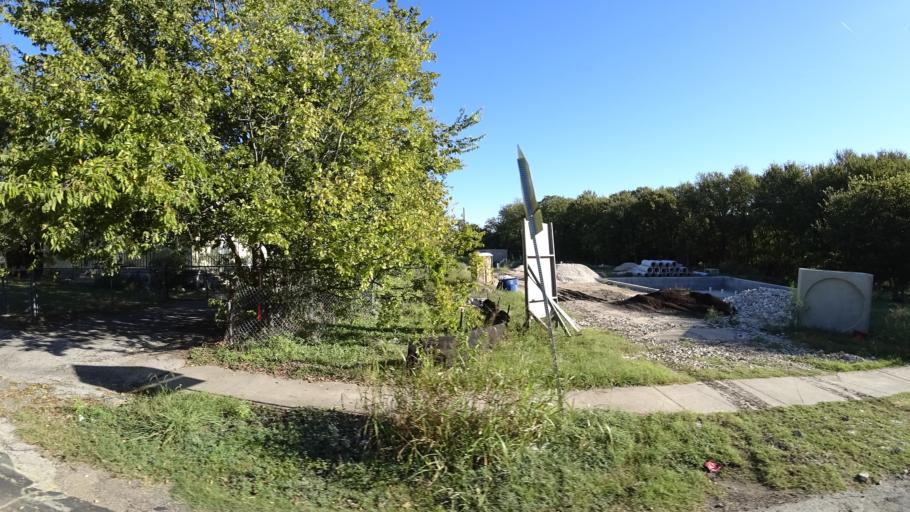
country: US
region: Texas
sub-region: Travis County
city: Austin
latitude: 30.3040
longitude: -97.6801
